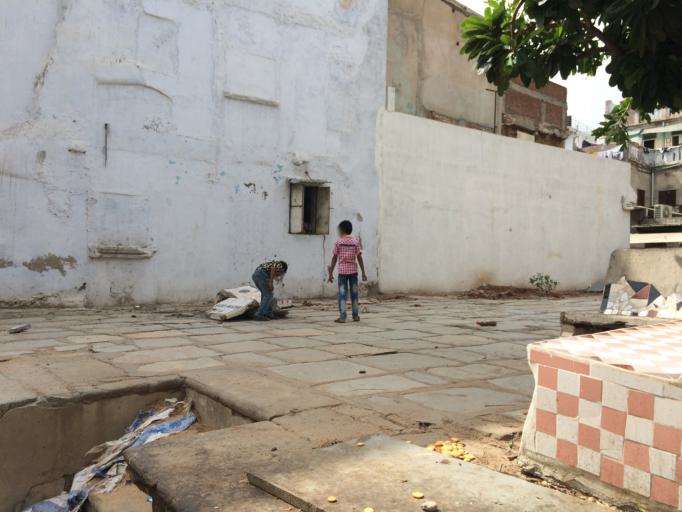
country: IN
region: Gujarat
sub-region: Ahmadabad
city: Ahmedabad
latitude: 23.0230
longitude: 72.5907
